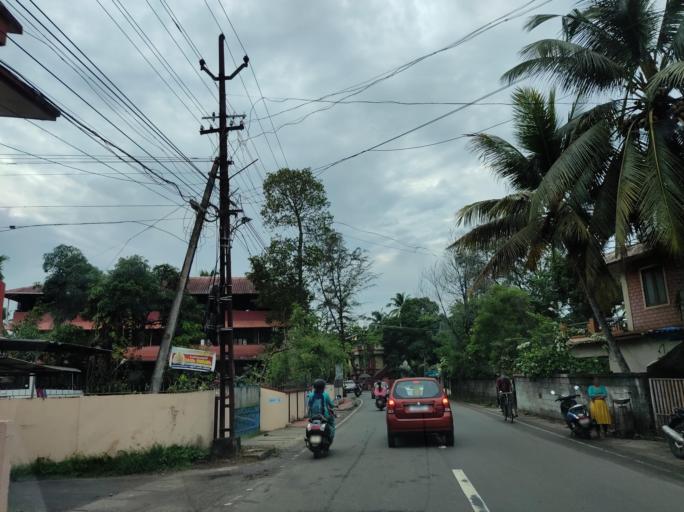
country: IN
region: Kerala
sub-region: Alappuzha
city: Mavelikara
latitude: 9.2521
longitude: 76.4860
